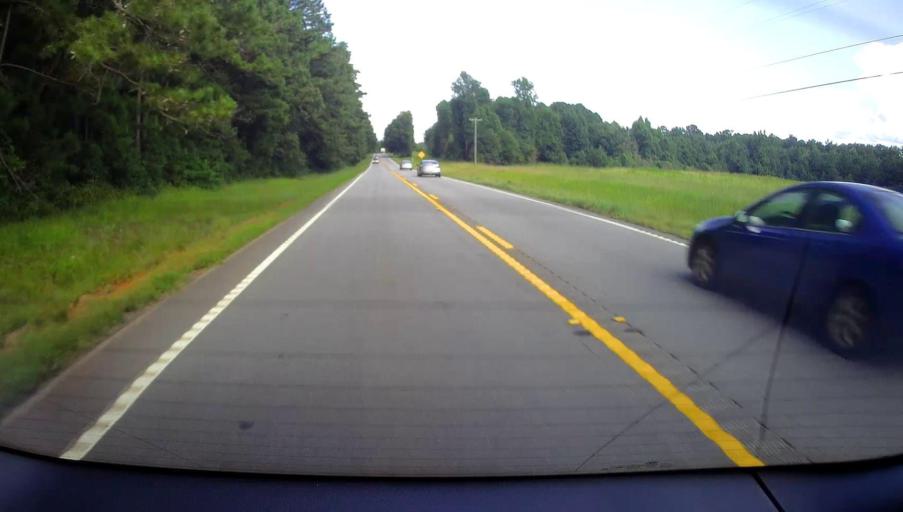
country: US
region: Georgia
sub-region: Meriwether County
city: Manchester
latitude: 32.9851
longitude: -84.5527
